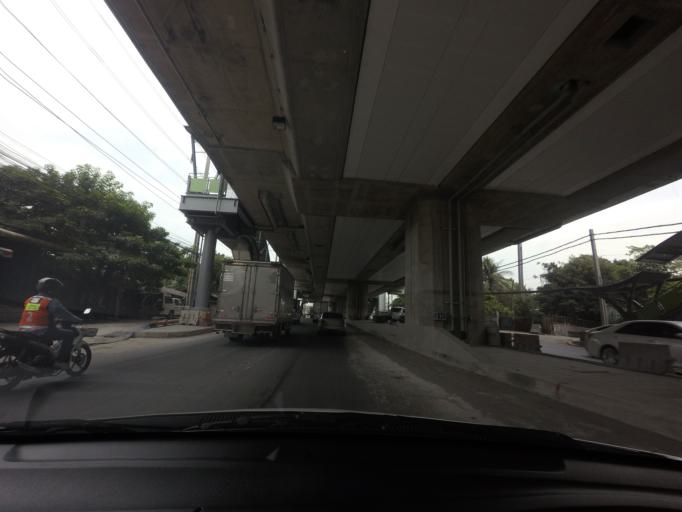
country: TH
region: Samut Prakan
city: Samut Prakan
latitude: 13.5926
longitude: 100.6087
